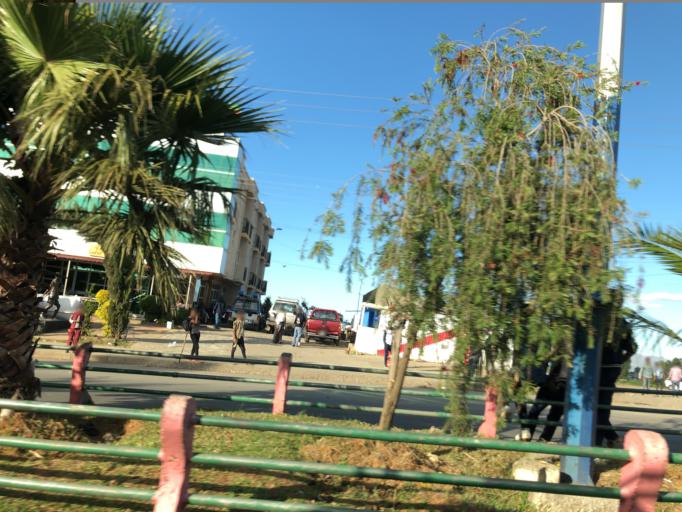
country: ET
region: Amhara
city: Debre Tabor
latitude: 11.8583
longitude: 38.0036
